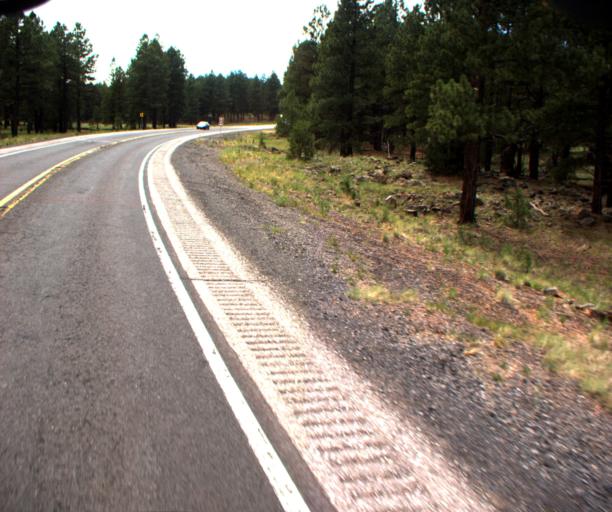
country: US
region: Arizona
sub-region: Coconino County
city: Flagstaff
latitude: 35.3986
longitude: -111.7565
